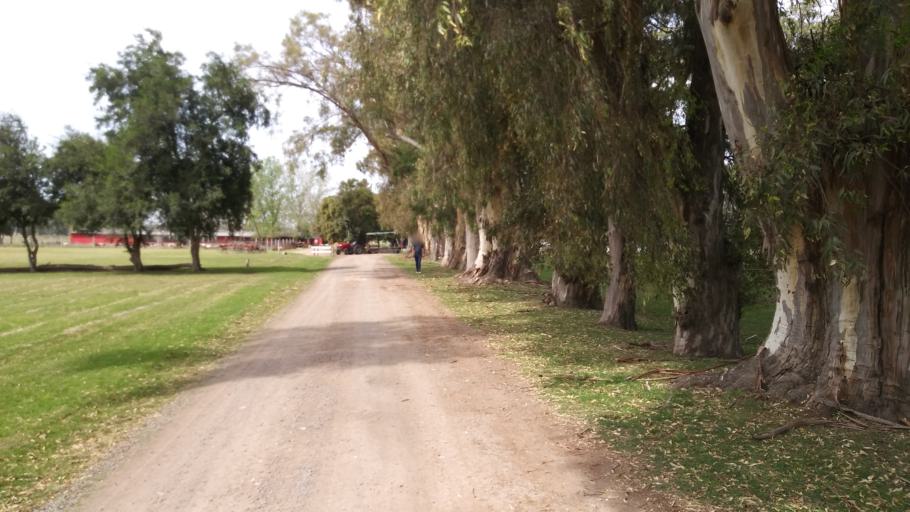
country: AR
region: Buenos Aires
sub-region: Partido de Lujan
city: Lujan
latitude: -34.5868
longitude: -59.1554
